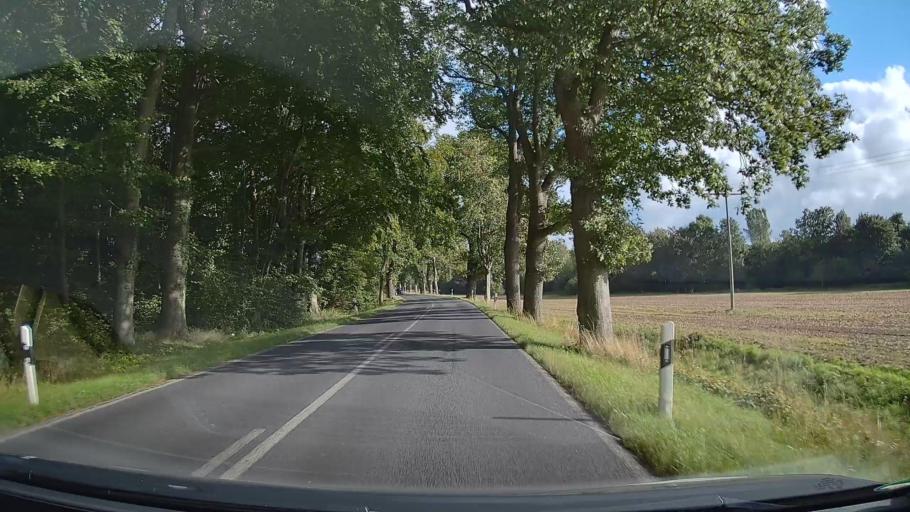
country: DE
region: Mecklenburg-Vorpommern
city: Putbus
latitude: 54.3841
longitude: 13.4749
